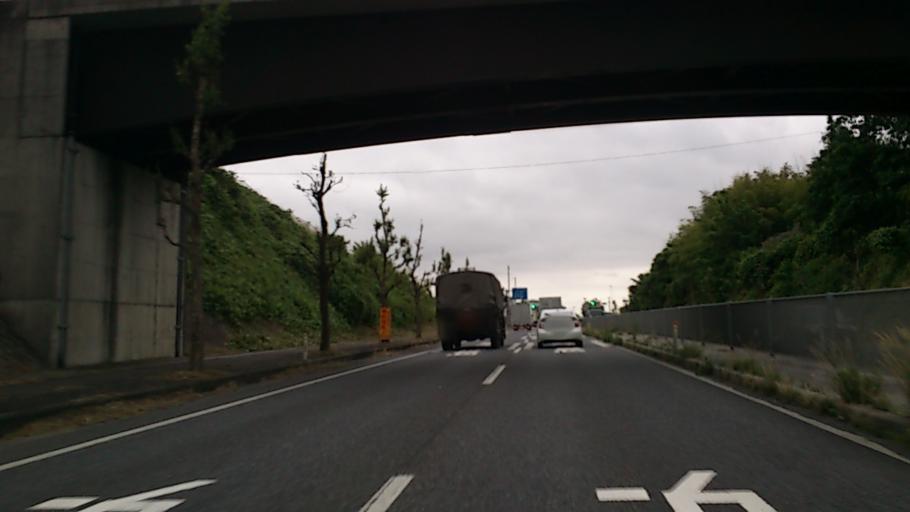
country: JP
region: Fukushima
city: Motomiya
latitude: 37.5074
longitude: 140.3946
